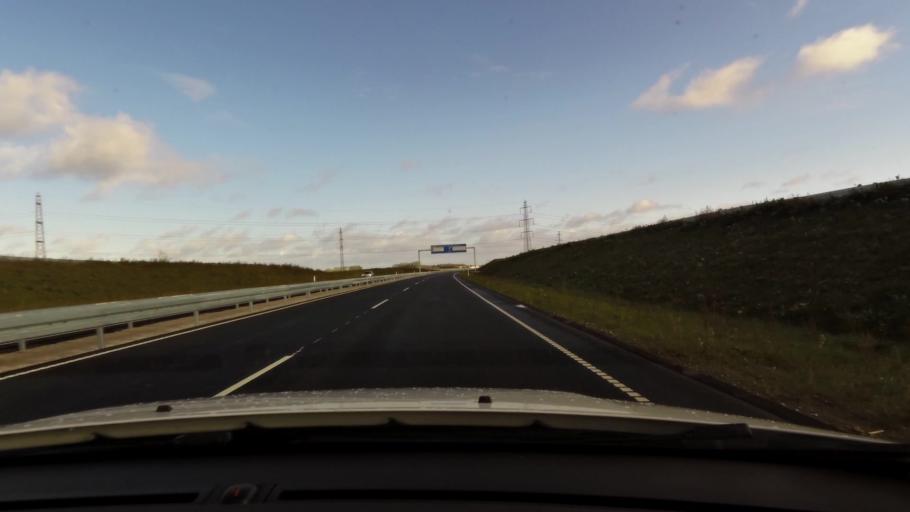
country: DK
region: Capital Region
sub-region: Frederikssund Kommune
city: Skibby
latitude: 55.7977
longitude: 11.9885
